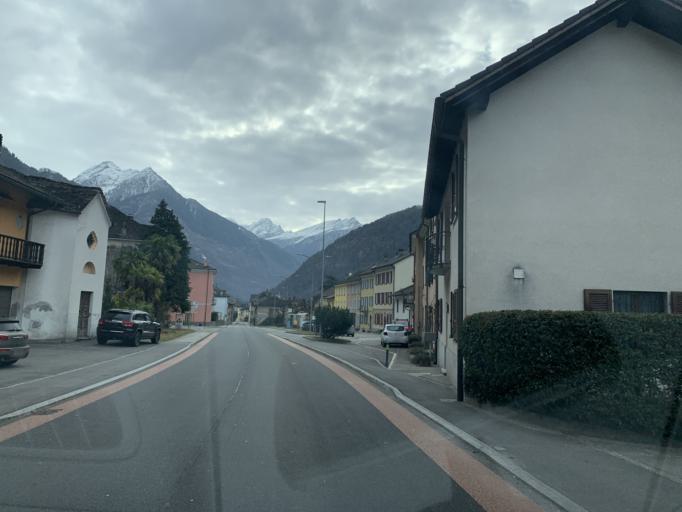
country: CH
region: Ticino
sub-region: Blenio District
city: Acquarossa
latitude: 46.4414
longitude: 8.9503
